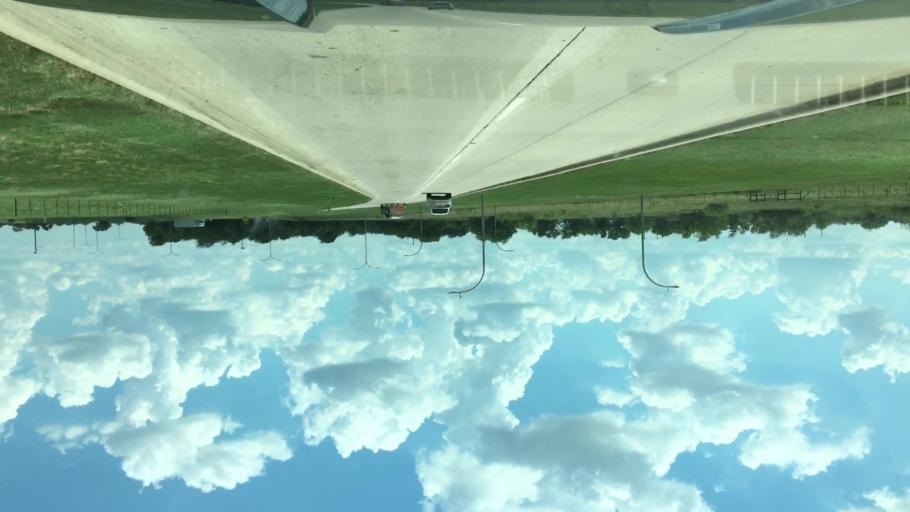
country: US
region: Texas
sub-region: Tarrant County
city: Haslet
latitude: 32.9723
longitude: -97.3173
